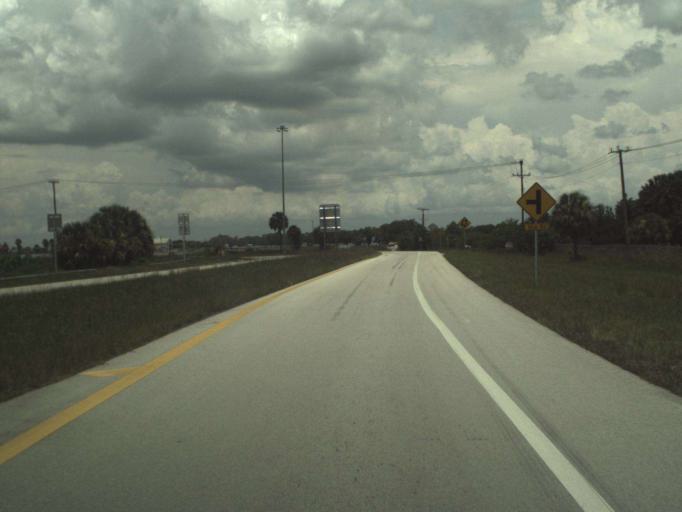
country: US
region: Florida
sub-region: Saint Lucie County
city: Lakewood Park
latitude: 27.5218
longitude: -80.4544
